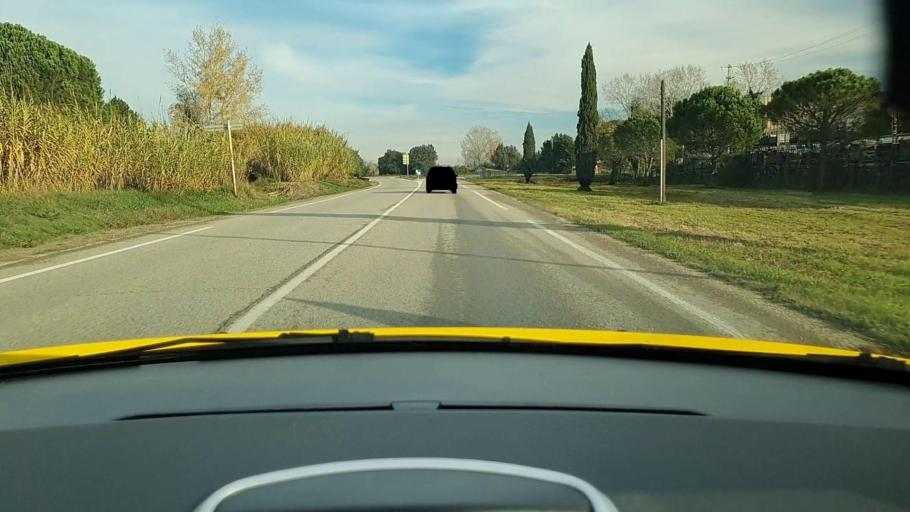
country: FR
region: Languedoc-Roussillon
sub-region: Departement du Gard
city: Fourques
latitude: 43.6976
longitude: 4.6002
